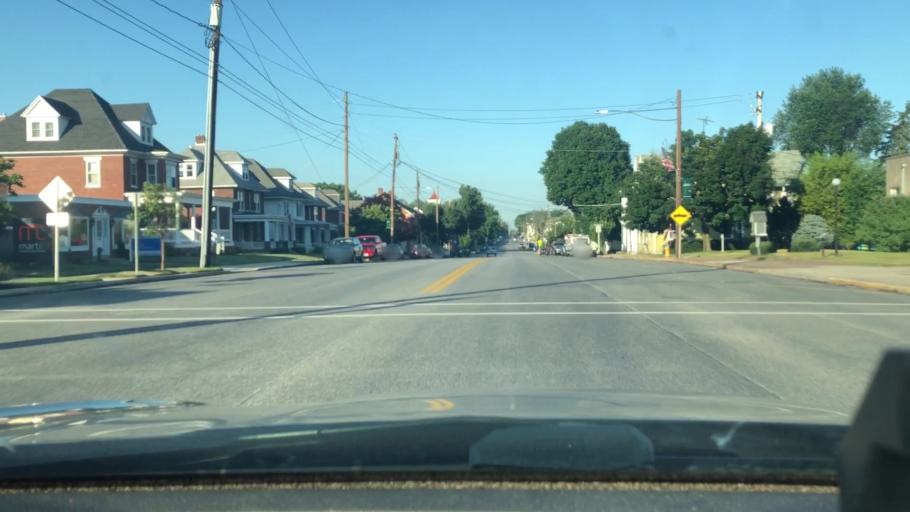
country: US
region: Pennsylvania
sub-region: Cumberland County
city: Shiremanstown
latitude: 40.2226
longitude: -76.9573
